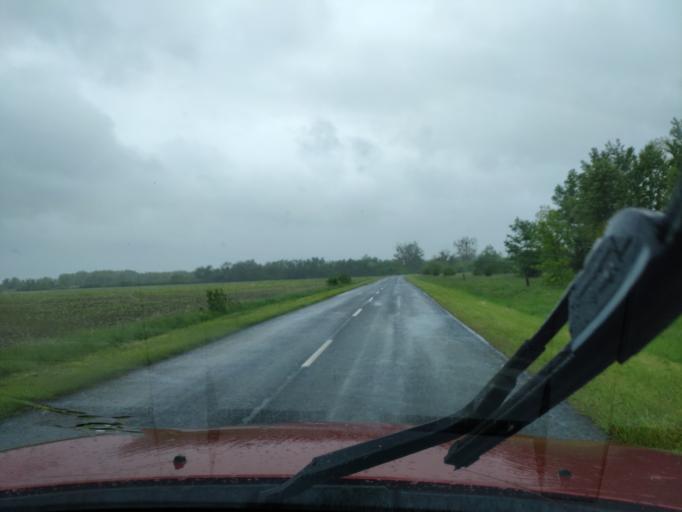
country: SK
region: Kosicky
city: Cierna nad Tisou
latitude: 48.4256
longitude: 22.1174
